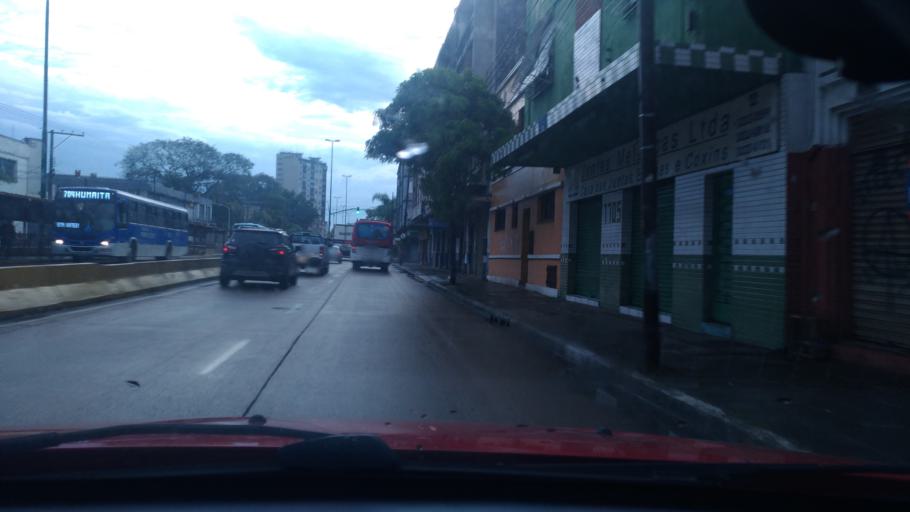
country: BR
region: Rio Grande do Sul
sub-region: Porto Alegre
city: Porto Alegre
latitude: -30.0167
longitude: -51.2075
